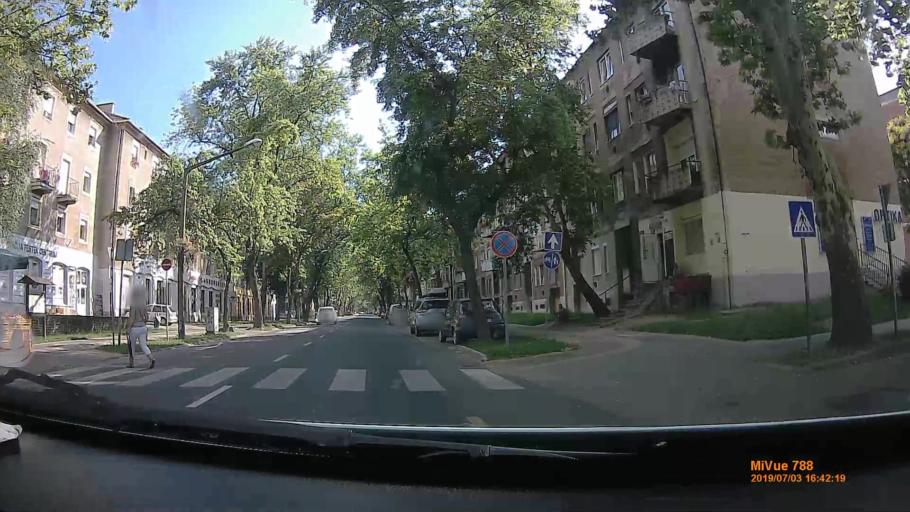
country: HU
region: Borsod-Abauj-Zemplen
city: Kazincbarcika
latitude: 48.2532
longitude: 20.6194
